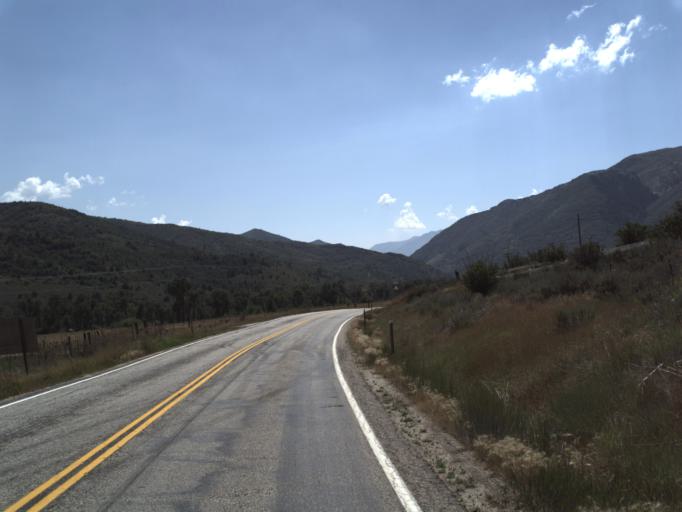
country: US
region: Utah
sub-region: Weber County
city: Wolf Creek
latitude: 41.2981
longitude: -111.6195
